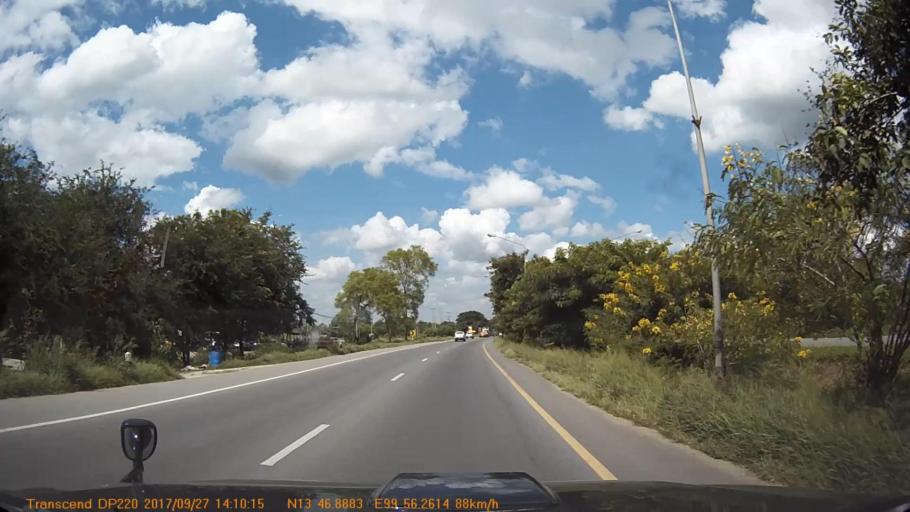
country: TH
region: Ratchaburi
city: Ban Pong
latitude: 13.7816
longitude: 99.9378
